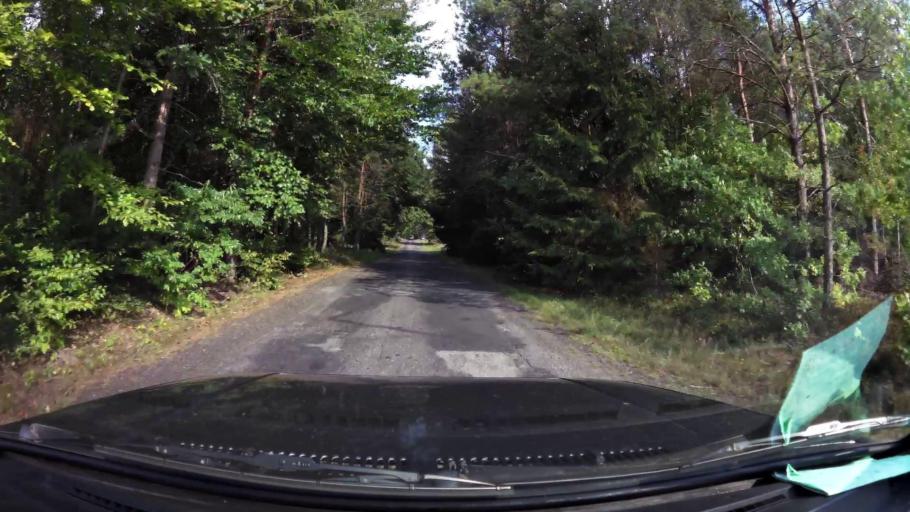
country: PL
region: West Pomeranian Voivodeship
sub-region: Powiat koszalinski
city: Bobolice
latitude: 54.0909
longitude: 16.4850
